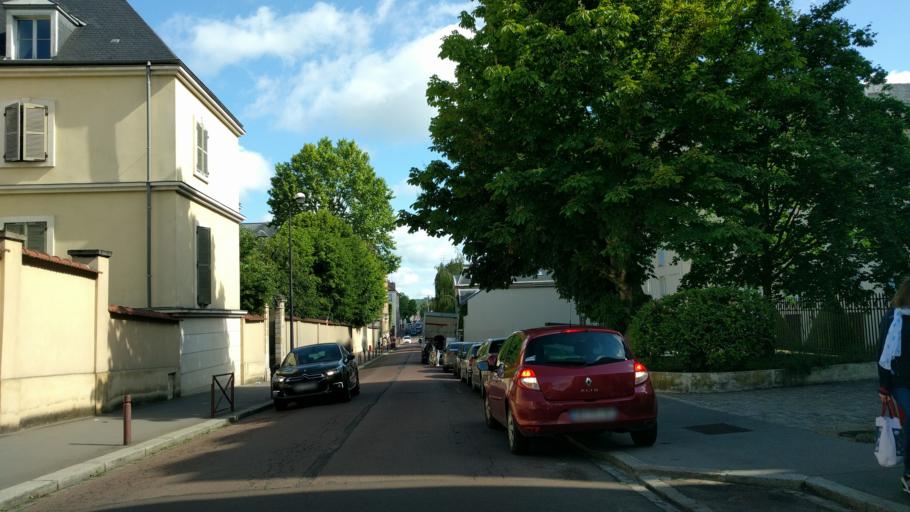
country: FR
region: Ile-de-France
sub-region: Departement des Yvelines
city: Versailles
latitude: 48.8069
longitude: 2.1398
